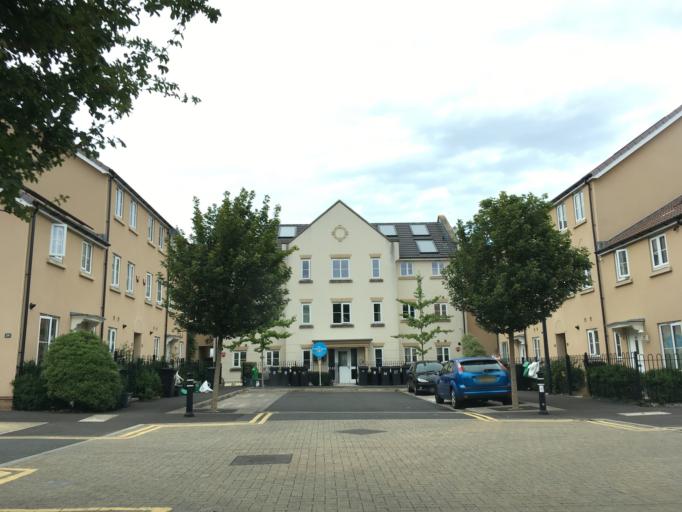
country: GB
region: England
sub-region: South Gloucestershire
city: Stoke Gifford
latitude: 51.4974
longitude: -2.5545
